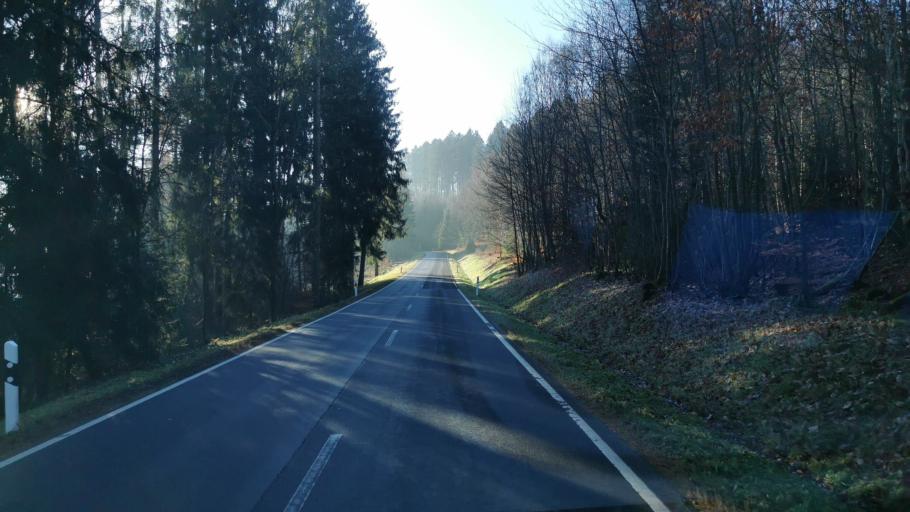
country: DE
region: Rheinland-Pfalz
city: Weidenbach
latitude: 50.1253
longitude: 6.7043
